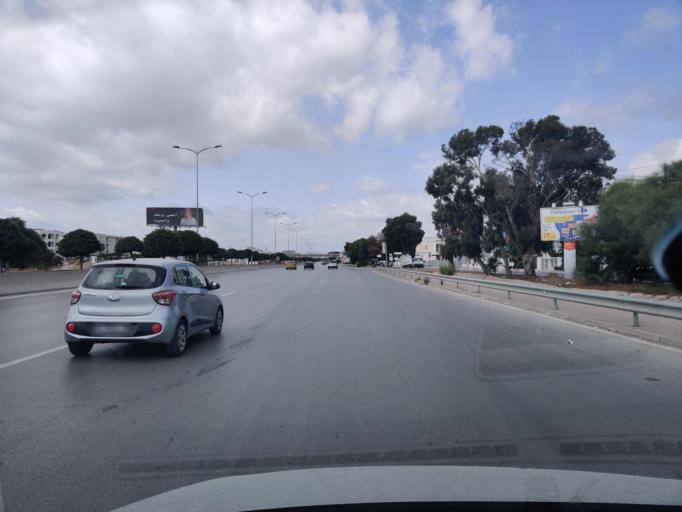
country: TN
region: Tunis
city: Al Marsa
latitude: 36.8691
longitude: 10.3093
